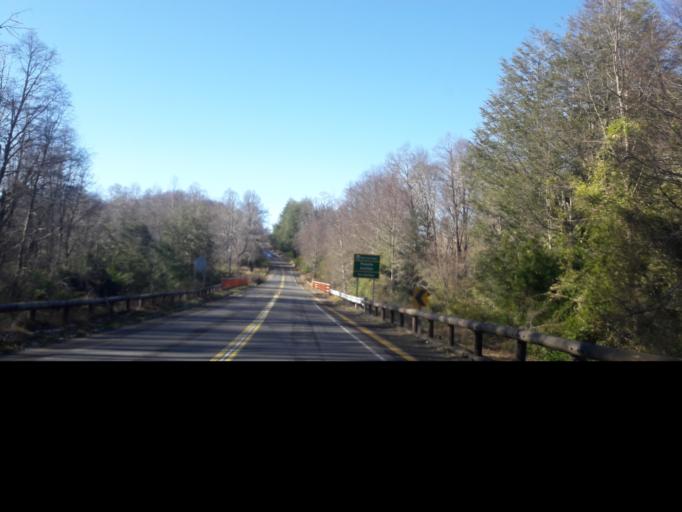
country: CL
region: Araucania
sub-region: Provincia de Malleco
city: Victoria
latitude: -38.3319
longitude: -71.9741
